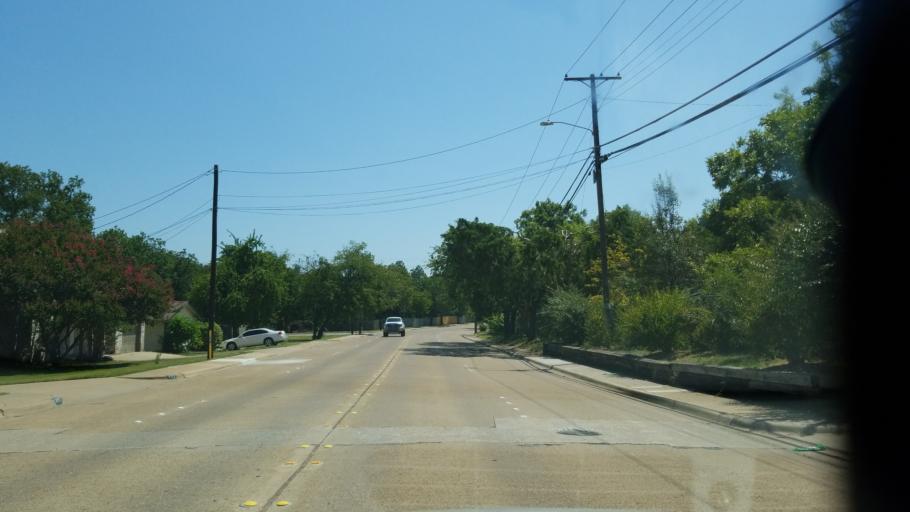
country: US
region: Texas
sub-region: Dallas County
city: Duncanville
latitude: 32.6517
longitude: -96.9036
